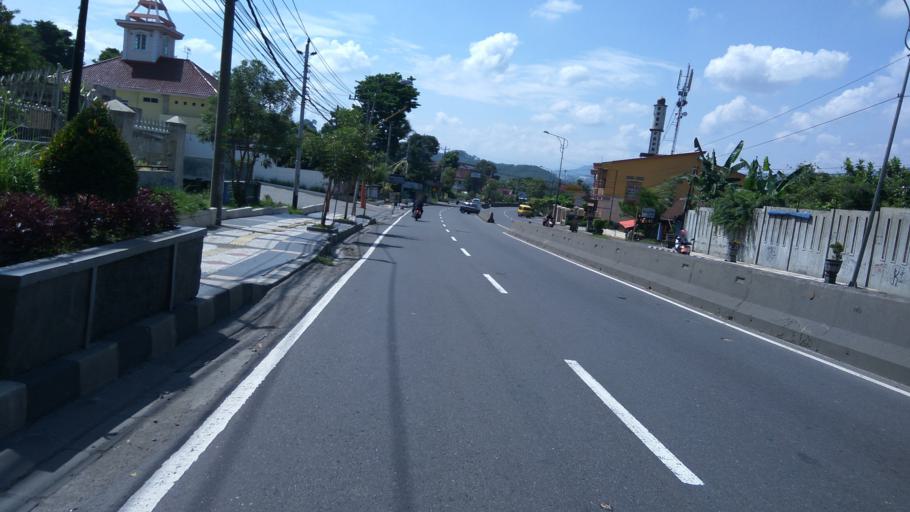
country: ID
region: Central Java
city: Ungaran
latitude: -7.1144
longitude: 110.4131
